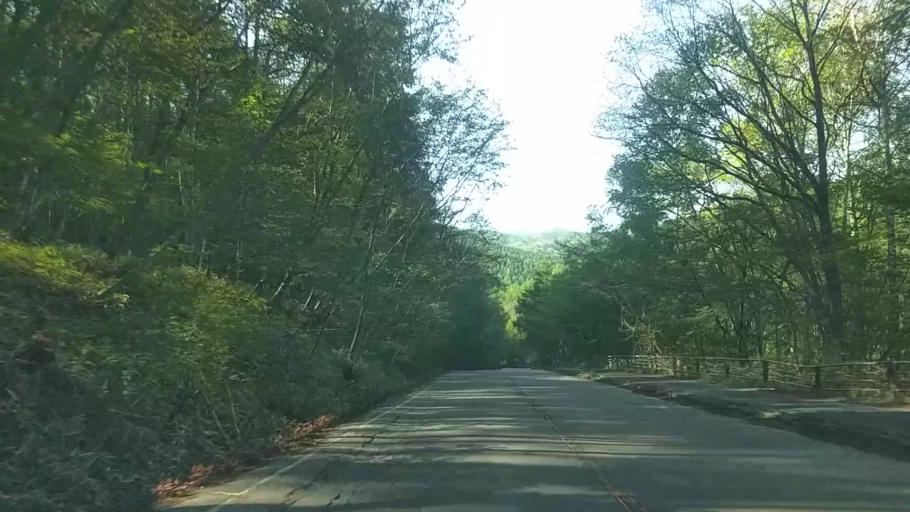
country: JP
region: Yamanashi
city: Nirasaki
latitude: 35.9078
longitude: 138.3937
